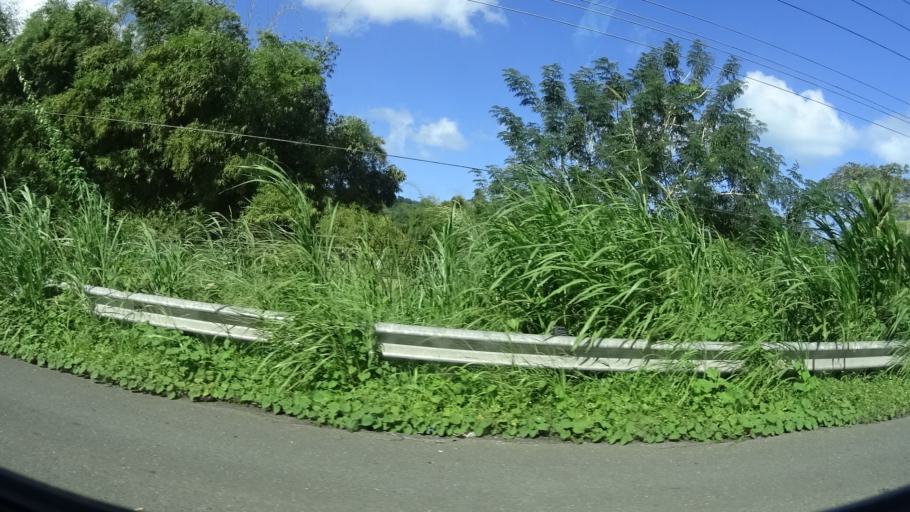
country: PR
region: Rio Grande
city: Palmer
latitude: 18.3723
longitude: -65.7641
